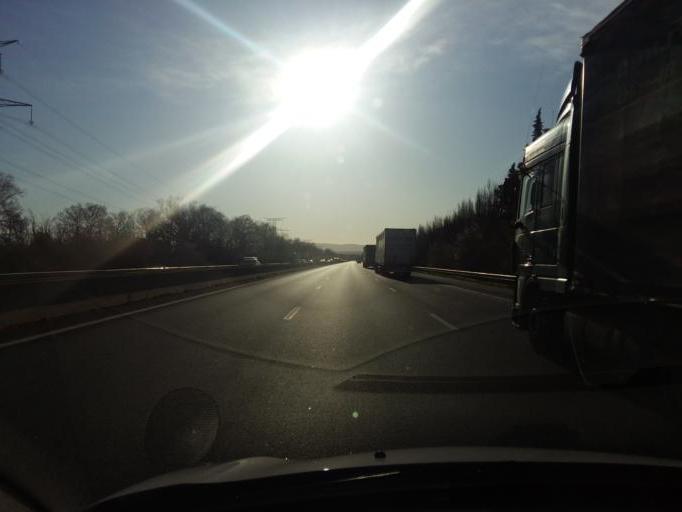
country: FR
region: Provence-Alpes-Cote d'Azur
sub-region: Departement des Bouches-du-Rhone
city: Cabannes
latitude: 43.8658
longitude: 4.9656
